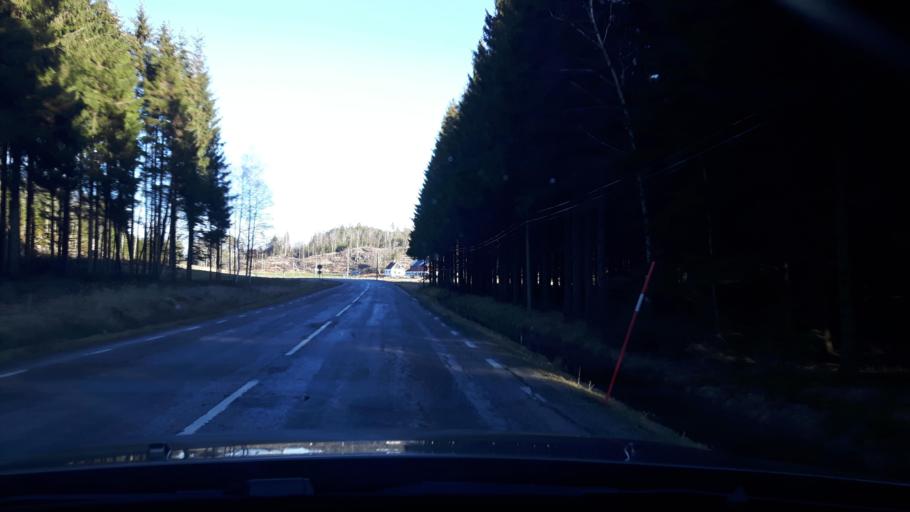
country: SE
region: Vaestra Goetaland
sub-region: Munkedals Kommun
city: Munkedal
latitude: 58.5505
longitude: 11.7179
